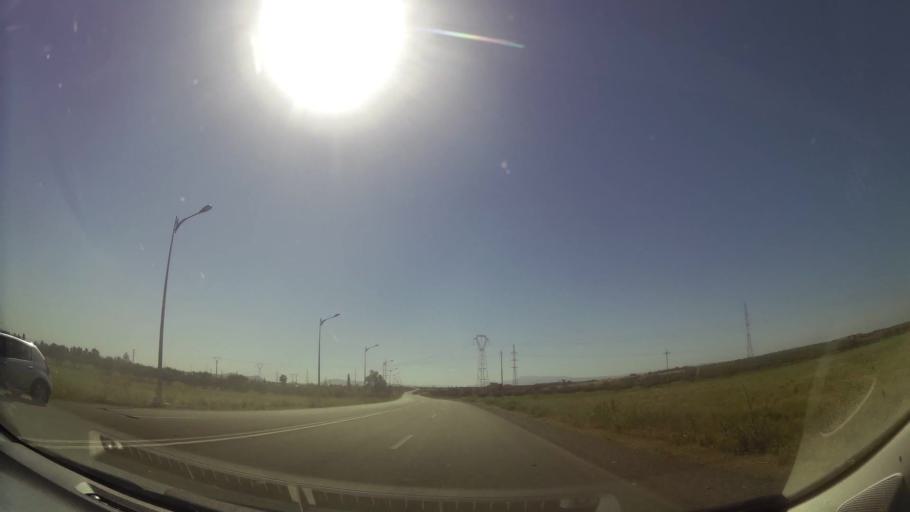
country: MA
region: Oriental
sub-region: Oujda-Angad
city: Oujda
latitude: 34.7394
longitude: -1.8873
